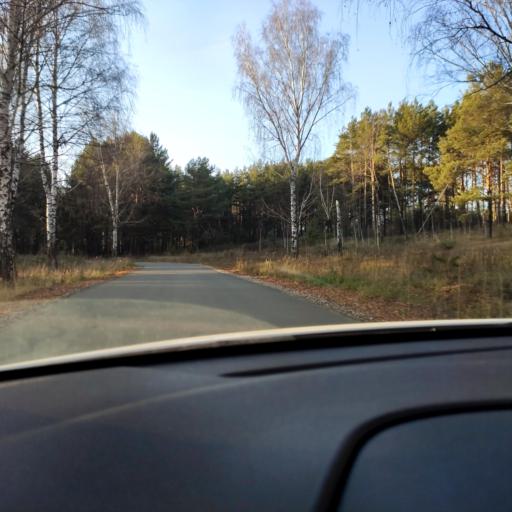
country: RU
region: Tatarstan
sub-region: Gorod Kazan'
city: Kazan
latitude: 55.8862
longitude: 49.0618
